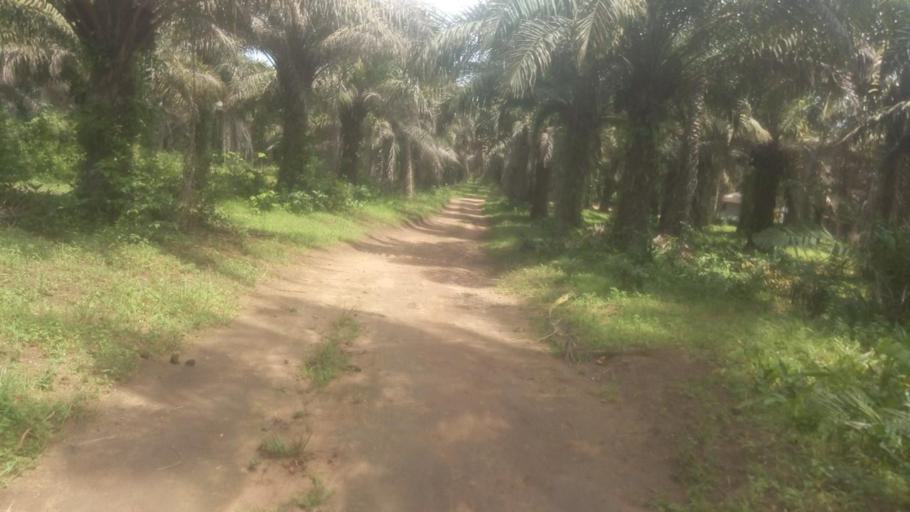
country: SL
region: Northern Province
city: Masoyila
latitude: 8.5454
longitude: -13.1604
